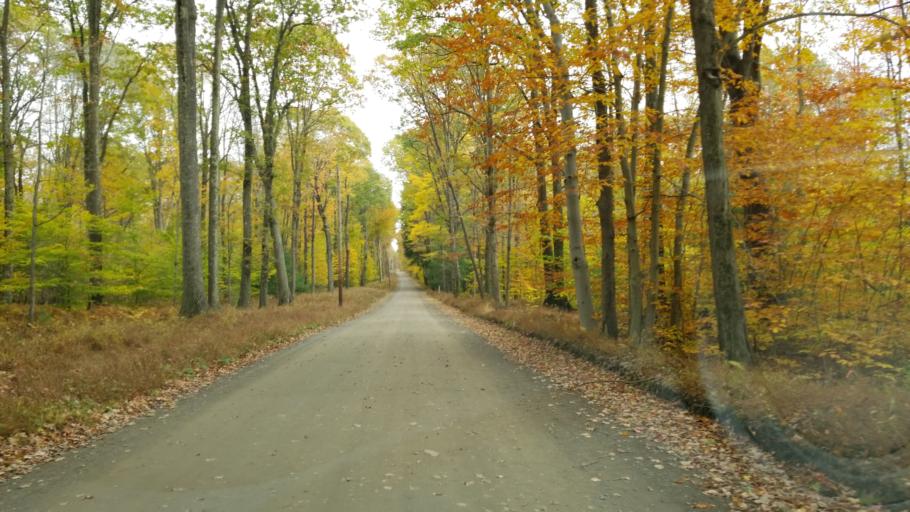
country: US
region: Pennsylvania
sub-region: Clearfield County
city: Shiloh
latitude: 41.1898
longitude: -78.3735
